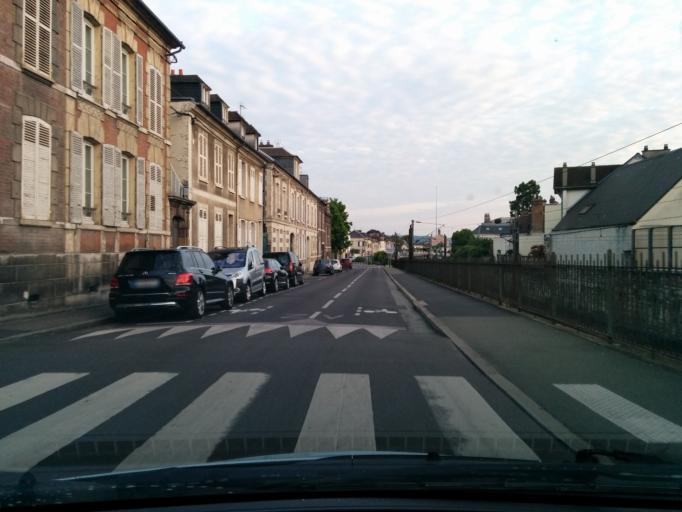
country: FR
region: Haute-Normandie
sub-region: Departement de l'Eure
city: Vernon
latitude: 49.0899
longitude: 1.4807
